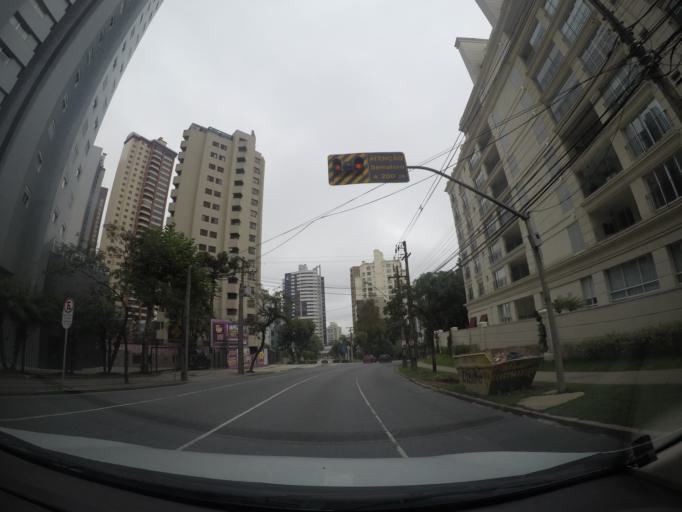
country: BR
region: Parana
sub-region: Curitiba
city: Curitiba
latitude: -25.4099
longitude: -49.2570
